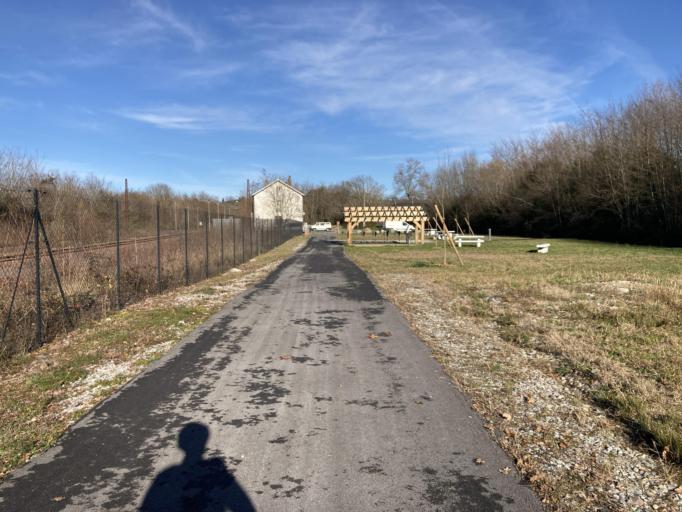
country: FR
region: Aquitaine
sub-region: Departement des Pyrenees-Atlantiques
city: Arudy
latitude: 43.1470
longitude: -0.4563
